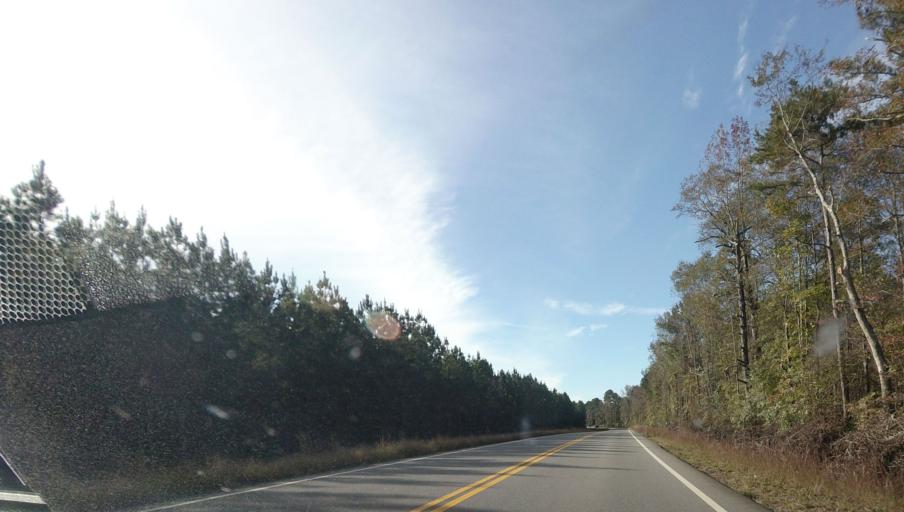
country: US
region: Georgia
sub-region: Upson County
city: Thomaston
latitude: 32.7188
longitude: -84.3105
